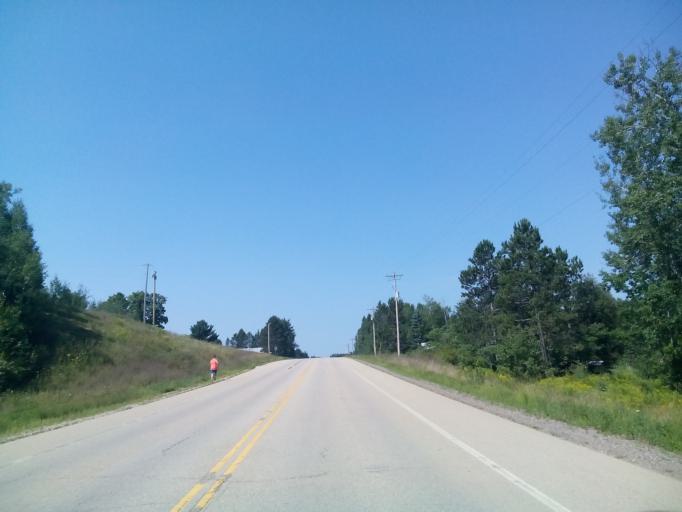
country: US
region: Wisconsin
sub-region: Menominee County
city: Legend Lake
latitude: 45.3012
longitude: -88.5048
